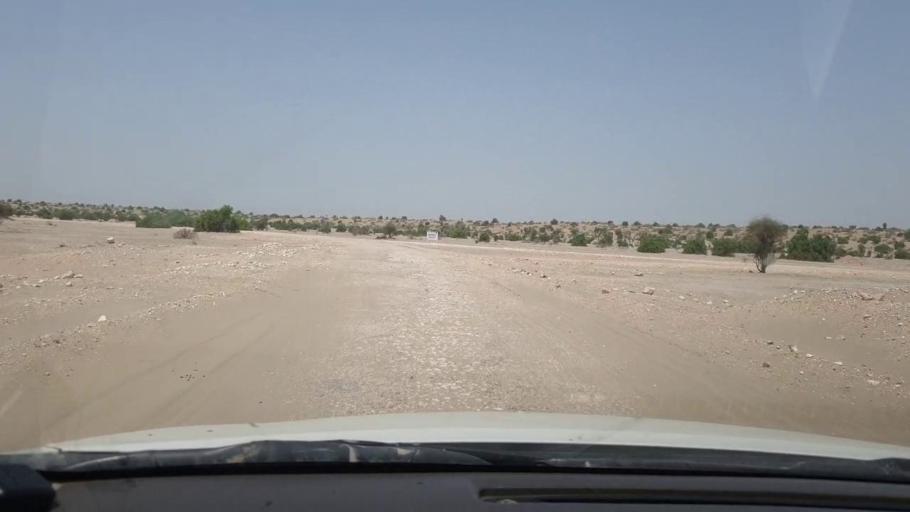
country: PK
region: Sindh
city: Kot Diji
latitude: 27.2844
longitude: 69.2338
